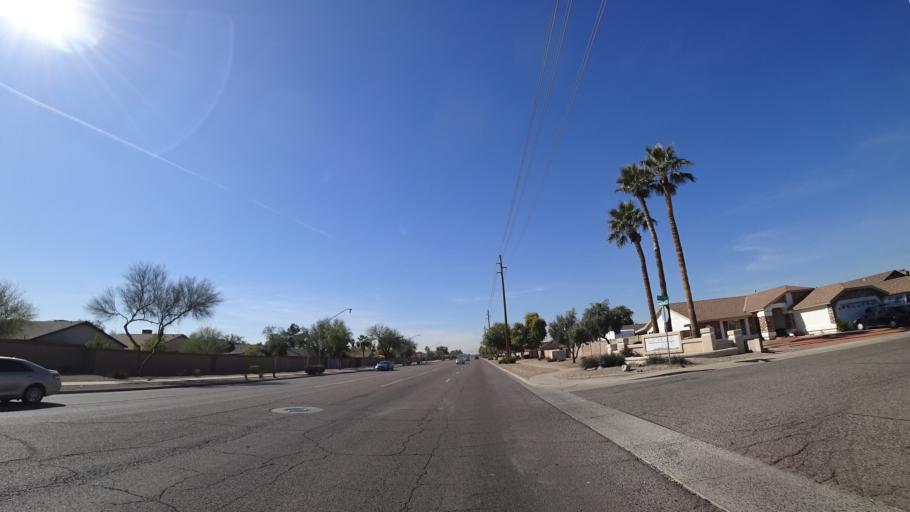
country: US
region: Arizona
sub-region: Maricopa County
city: Tolleson
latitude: 33.5089
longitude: -112.2422
